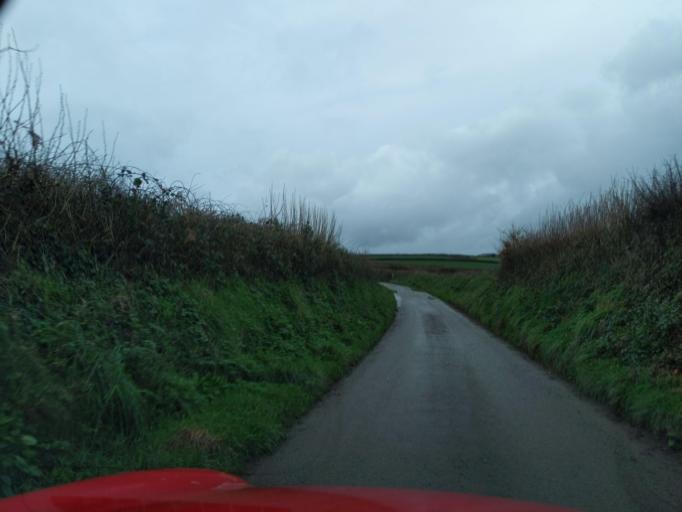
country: GB
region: England
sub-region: Cornwall
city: Duloe
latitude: 50.3476
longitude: -4.5364
